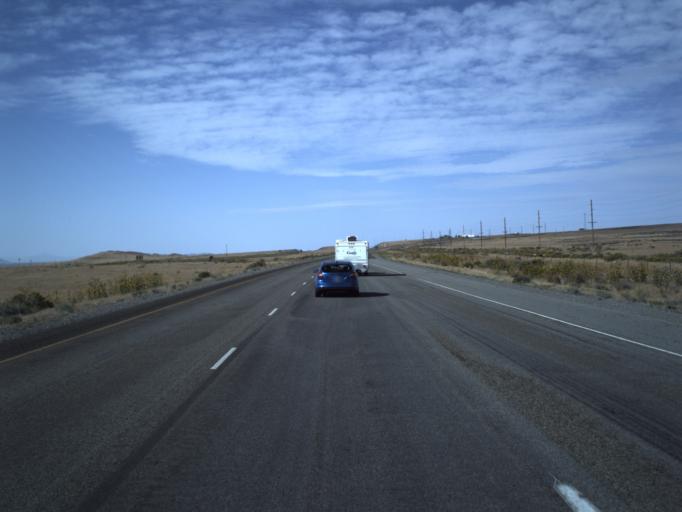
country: US
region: Utah
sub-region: Tooele County
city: Grantsville
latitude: 40.7660
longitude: -112.9919
